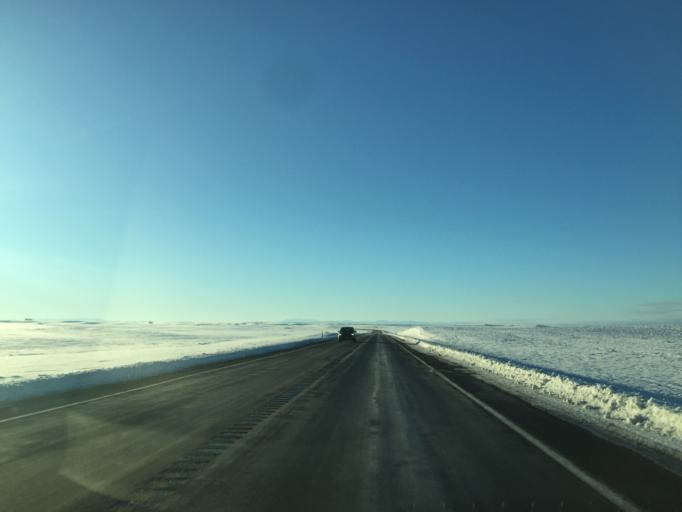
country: US
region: Washington
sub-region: Grant County
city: Soap Lake
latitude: 47.6199
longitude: -119.4519
